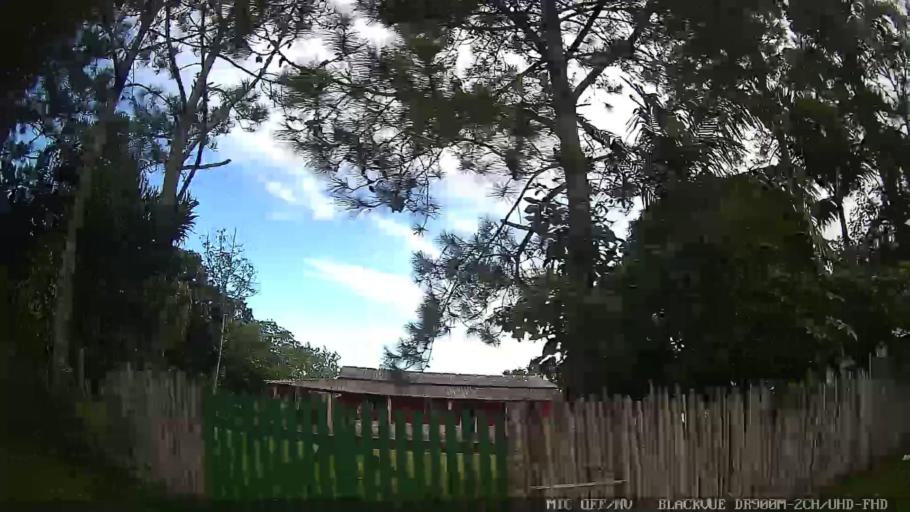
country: BR
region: Sao Paulo
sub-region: Iguape
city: Iguape
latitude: -24.6545
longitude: -47.4058
